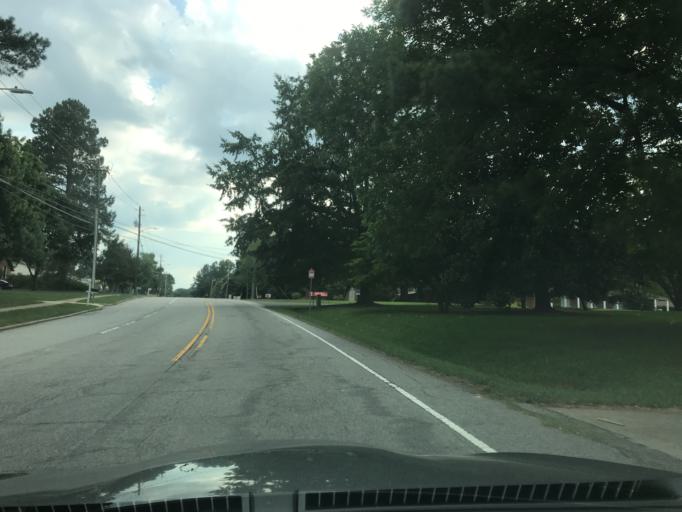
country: US
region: North Carolina
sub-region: Wake County
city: West Raleigh
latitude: 35.8257
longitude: -78.6966
